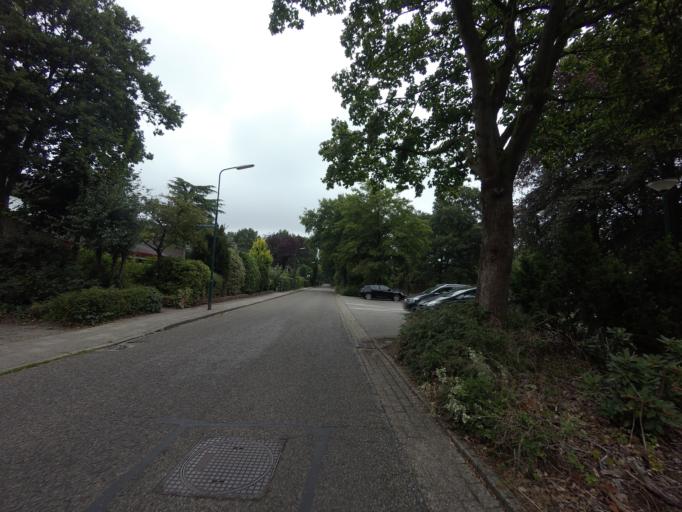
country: NL
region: Utrecht
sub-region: Gemeente Utrechtse Heuvelrug
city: Amerongen
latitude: 52.0029
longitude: 5.4662
